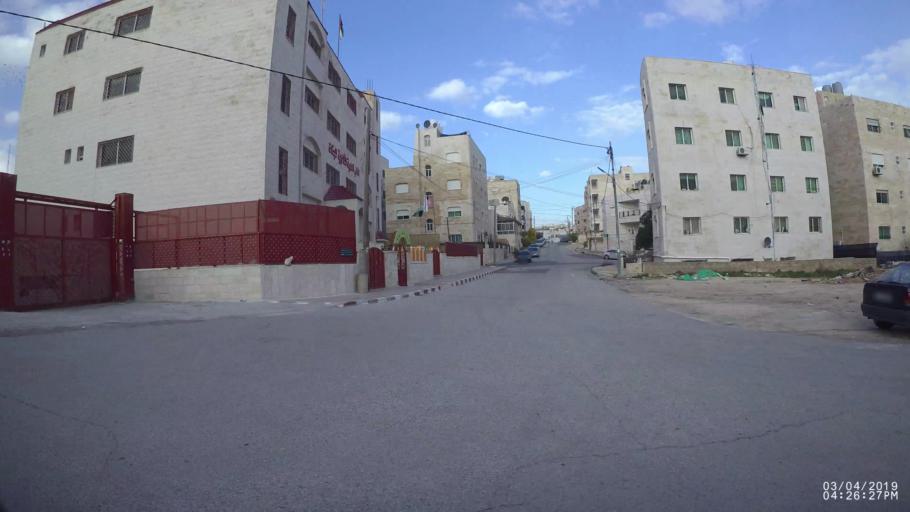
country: JO
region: Amman
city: Al Bunayyat ash Shamaliyah
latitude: 31.9133
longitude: 35.8887
